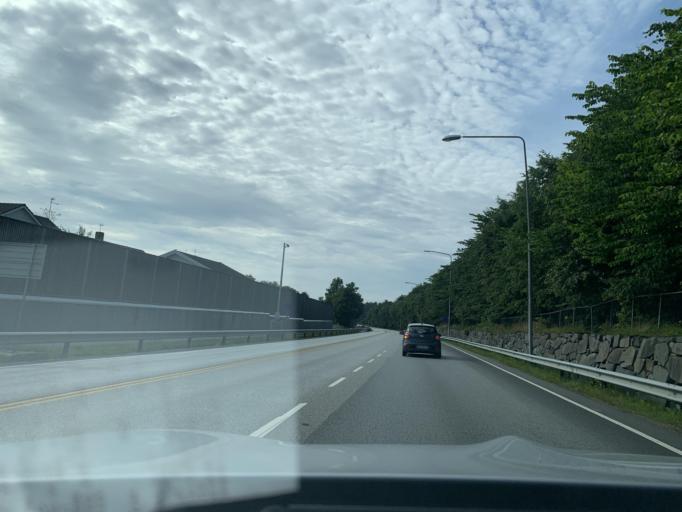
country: NO
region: Rogaland
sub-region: Stavanger
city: Stavanger
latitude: 58.9147
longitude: 5.7231
